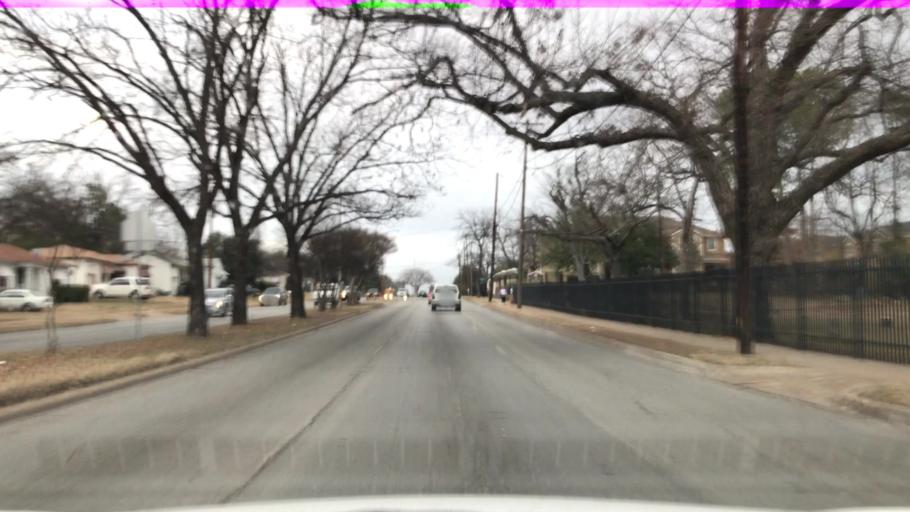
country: US
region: Texas
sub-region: Dallas County
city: Dallas
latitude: 32.7579
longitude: -96.7506
